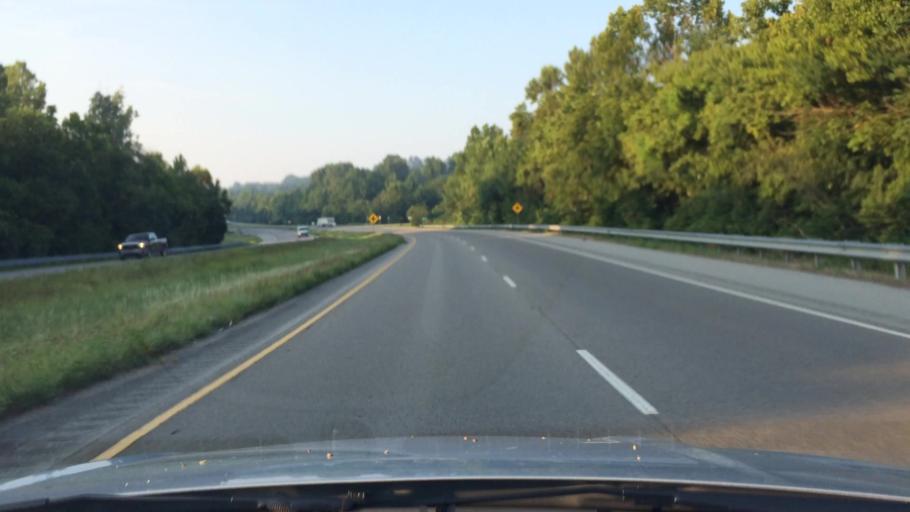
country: US
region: Tennessee
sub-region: Giles County
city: Pulaski
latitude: 35.1909
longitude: -87.0647
